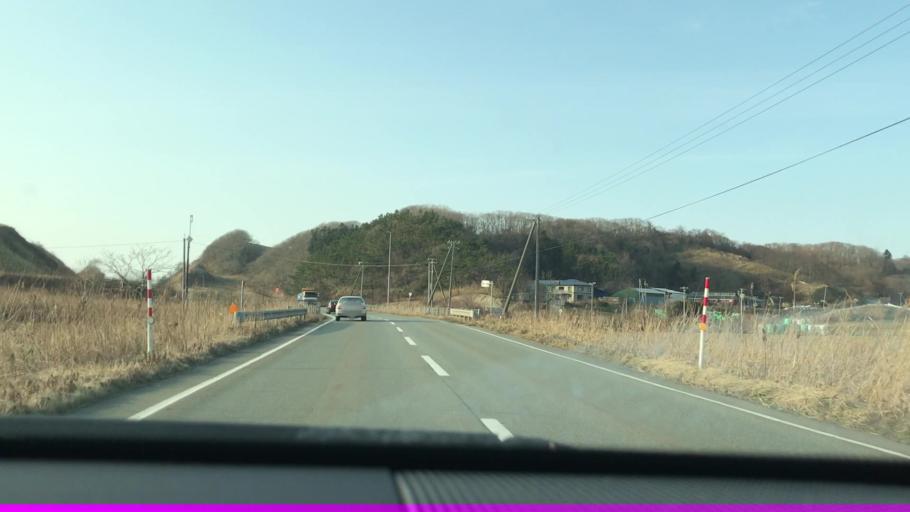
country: JP
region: Hokkaido
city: Shizunai-furukawacho
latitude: 42.2308
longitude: 142.6119
